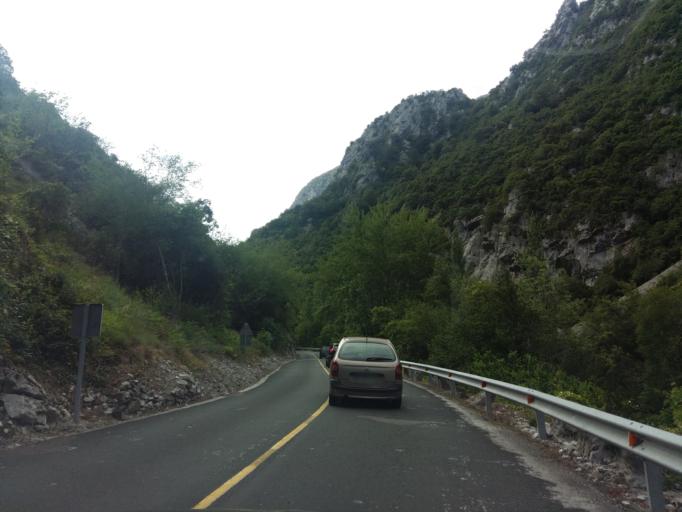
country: ES
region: Cantabria
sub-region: Provincia de Cantabria
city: Tresviso
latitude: 43.2474
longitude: -4.5907
